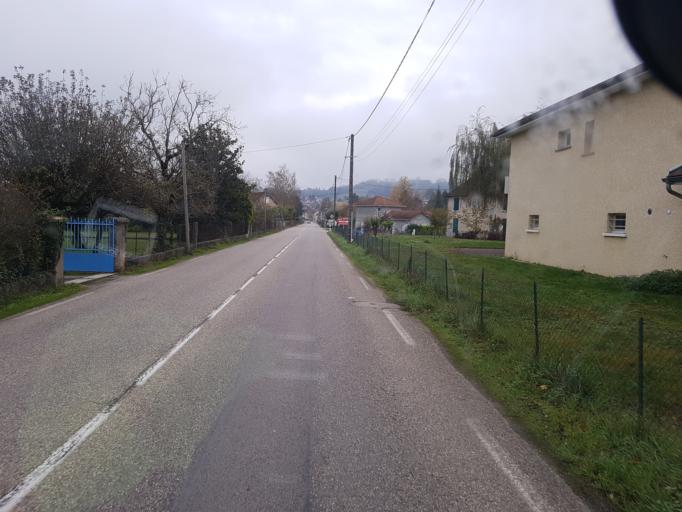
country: FR
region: Rhone-Alpes
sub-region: Departement de la Savoie
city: Saint-Genix-sur-Guiers
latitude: 45.5954
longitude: 5.6245
